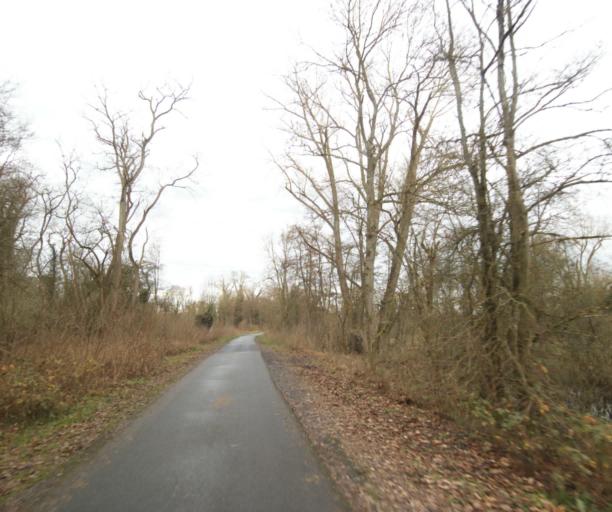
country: FR
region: Nord-Pas-de-Calais
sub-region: Departement du Nord
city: Hergnies
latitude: 50.4655
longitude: 3.5329
